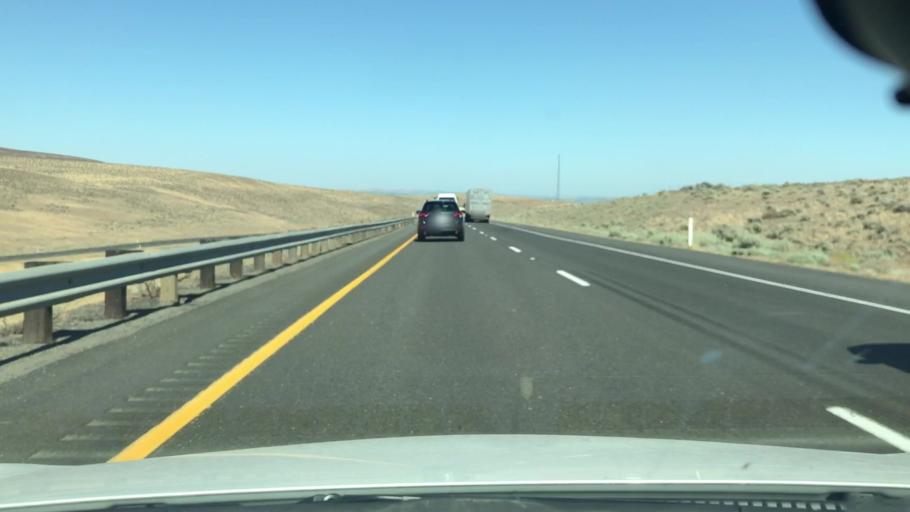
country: US
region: Washington
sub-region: Grant County
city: Mattawa
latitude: 46.9450
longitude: -120.0981
